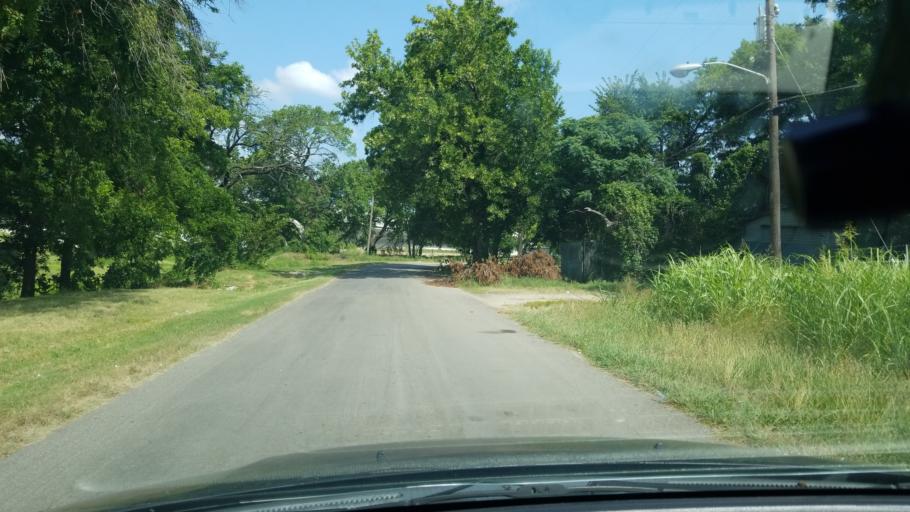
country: US
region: Texas
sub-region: Dallas County
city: Dallas
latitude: 32.7636
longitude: -96.8028
